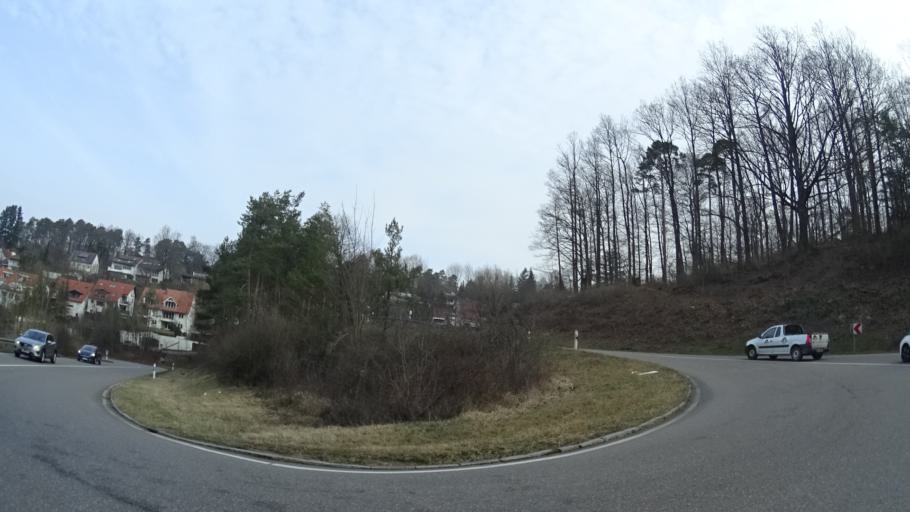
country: DE
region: Baden-Wuerttemberg
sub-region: Regierungsbezirk Stuttgart
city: Leonberg
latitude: 48.7898
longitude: 9.0385
